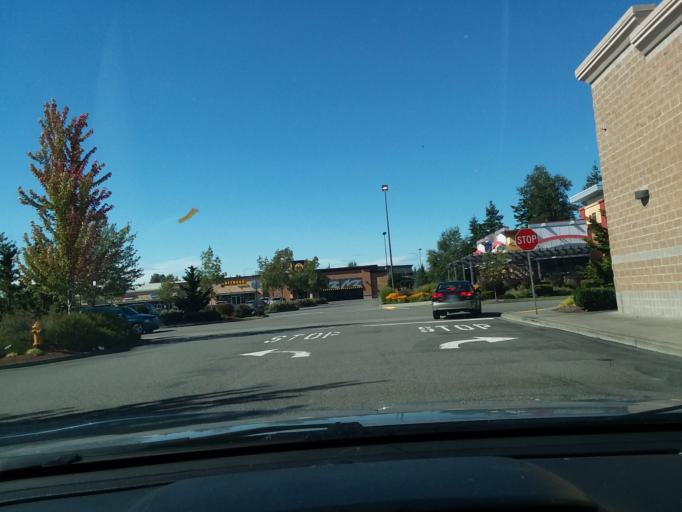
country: US
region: Washington
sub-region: Snohomish County
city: Smokey Point
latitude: 48.1496
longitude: -122.1900
